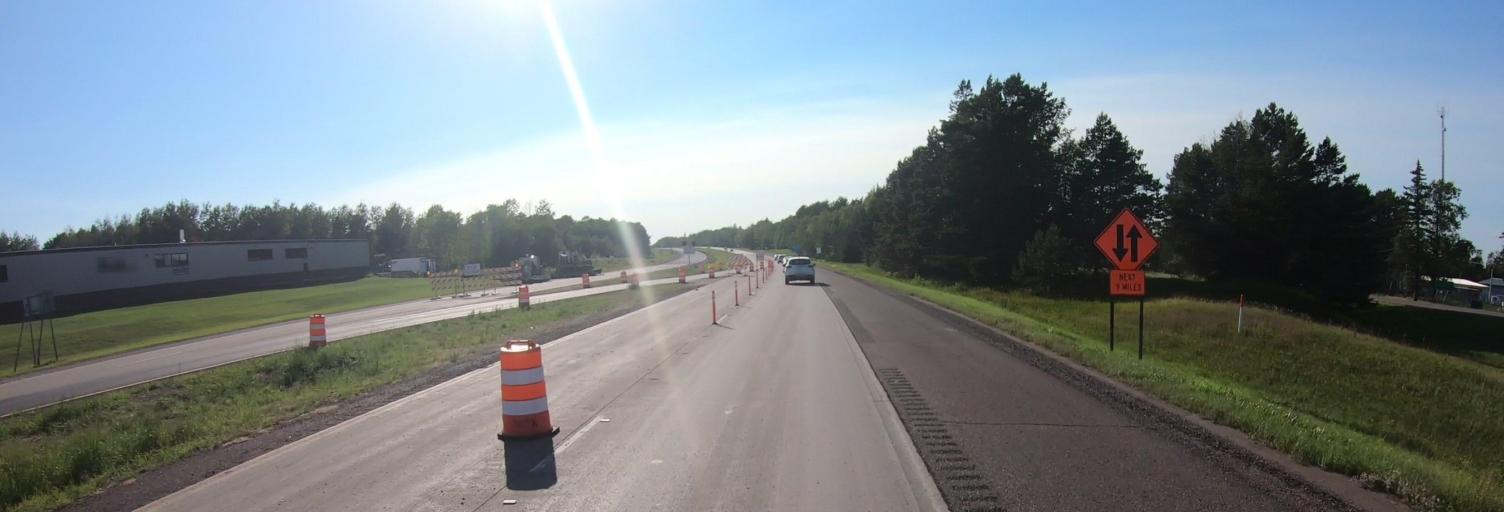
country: US
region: Minnesota
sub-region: Saint Louis County
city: Hermantown
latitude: 46.8513
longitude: -92.2870
